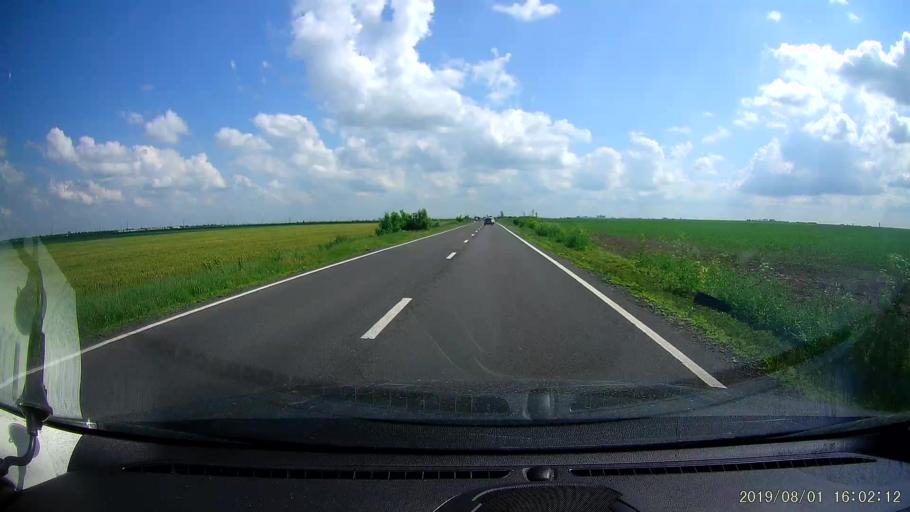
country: RO
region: Ialomita
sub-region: Comuna Ciulnita
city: Ciulnita
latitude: 44.4943
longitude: 27.3881
